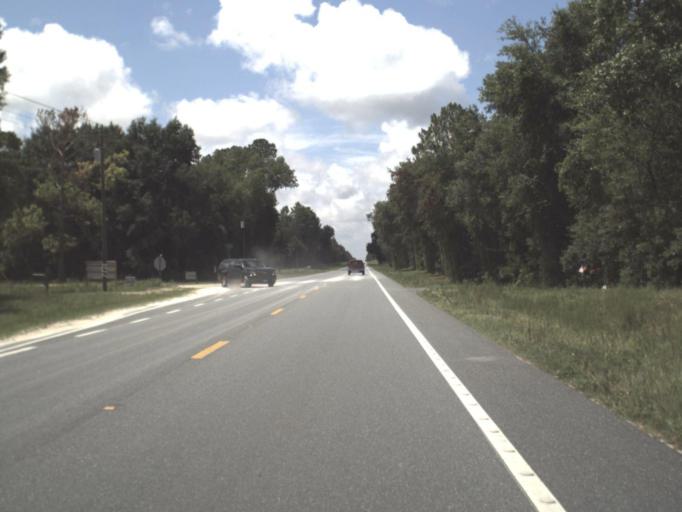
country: US
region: Florida
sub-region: Gilchrist County
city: Trenton
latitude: 29.8112
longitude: -82.8671
